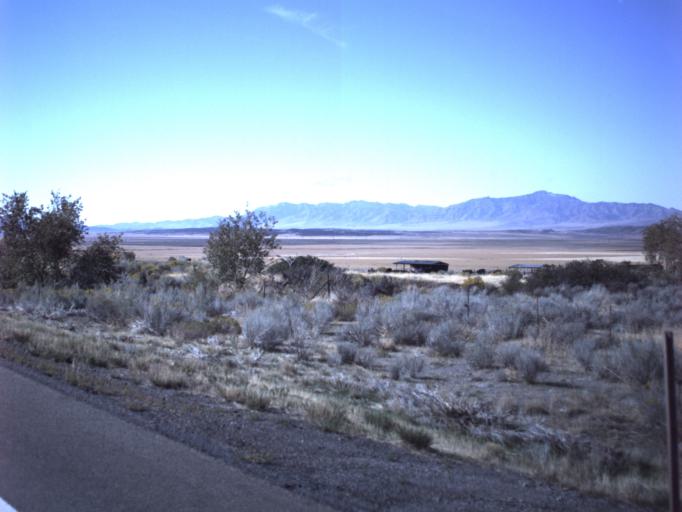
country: US
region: Utah
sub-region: Juab County
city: Nephi
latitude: 39.5119
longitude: -111.8688
